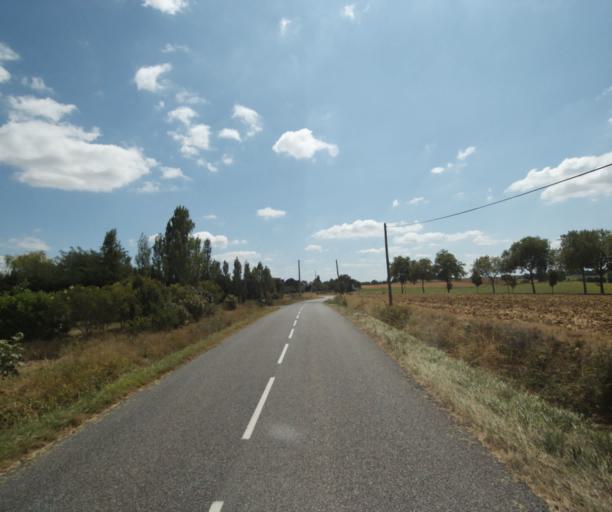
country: FR
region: Midi-Pyrenees
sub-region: Departement de la Haute-Garonne
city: Saint-Felix-Lauragais
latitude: 43.4627
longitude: 1.8284
